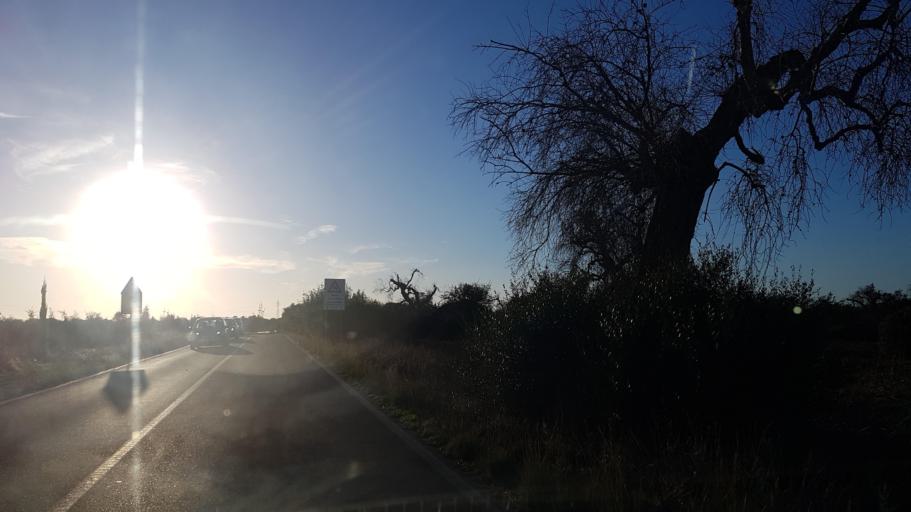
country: IT
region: Apulia
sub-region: Provincia di Lecce
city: Giorgilorio
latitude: 40.4191
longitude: 18.2099
